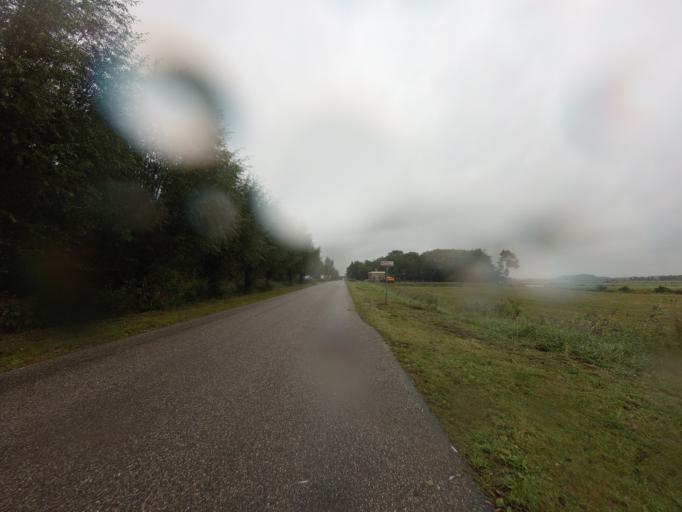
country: NL
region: Friesland
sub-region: Gemeente Tytsjerksteradiel
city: Garyp
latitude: 53.1343
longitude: 5.9547
